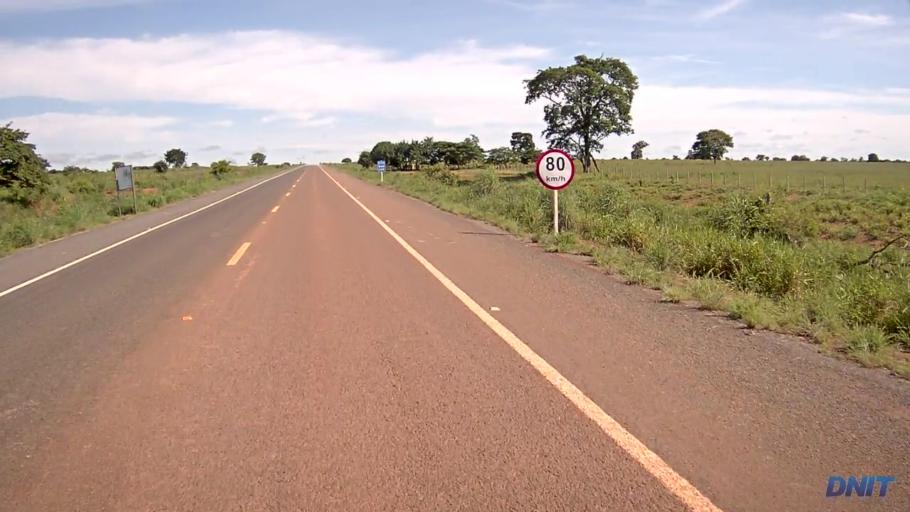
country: BR
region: Goias
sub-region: Sao Miguel Do Araguaia
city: Sao Miguel do Araguaia
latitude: -13.4950
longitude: -50.1078
